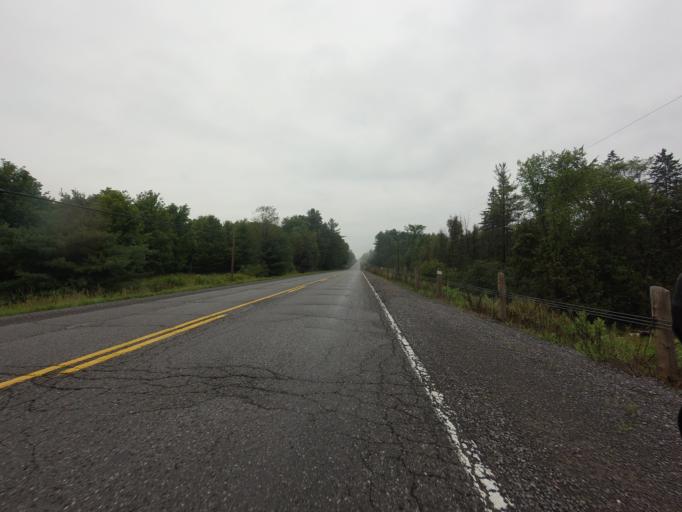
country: CA
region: Ontario
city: Carleton Place
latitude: 45.1454
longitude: -76.3185
